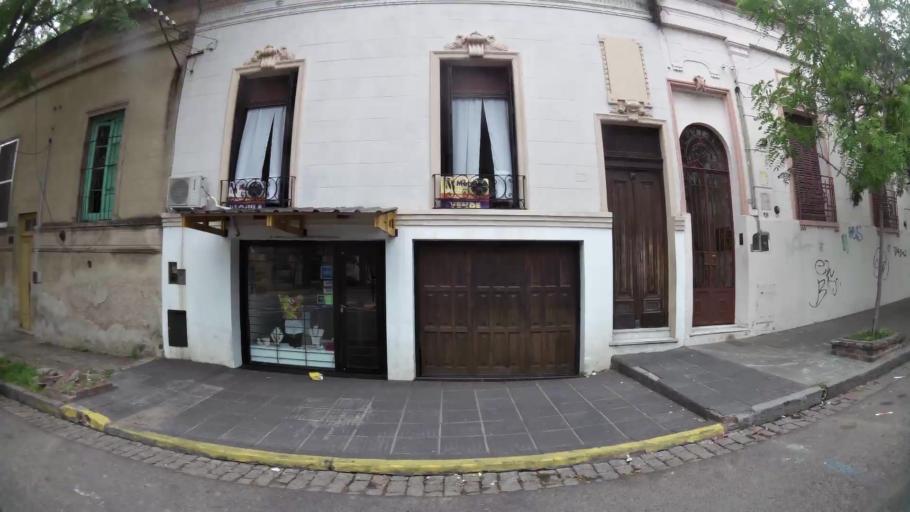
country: AR
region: Buenos Aires
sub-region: Partido de Campana
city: Campana
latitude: -34.1626
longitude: -58.9579
